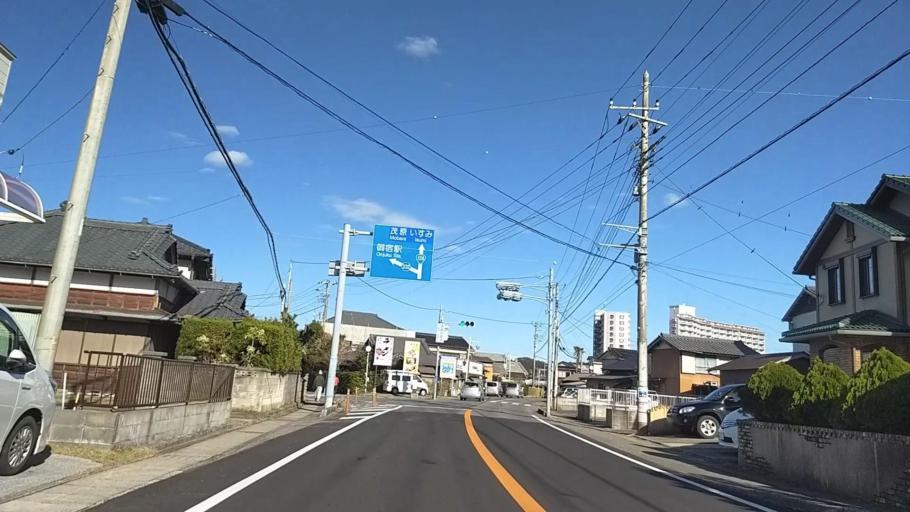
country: JP
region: Chiba
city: Katsuura
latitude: 35.1841
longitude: 140.3502
